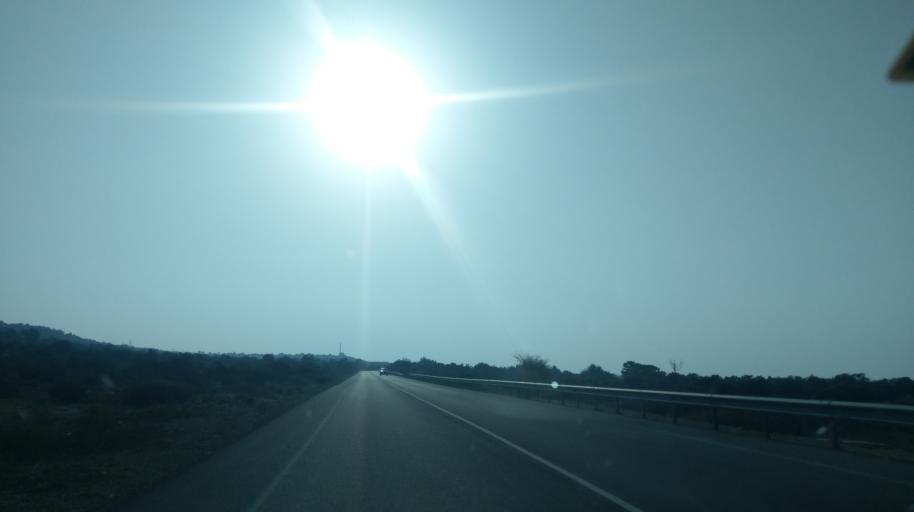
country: CY
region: Ammochostos
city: Leonarisso
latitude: 35.5520
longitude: 34.2103
